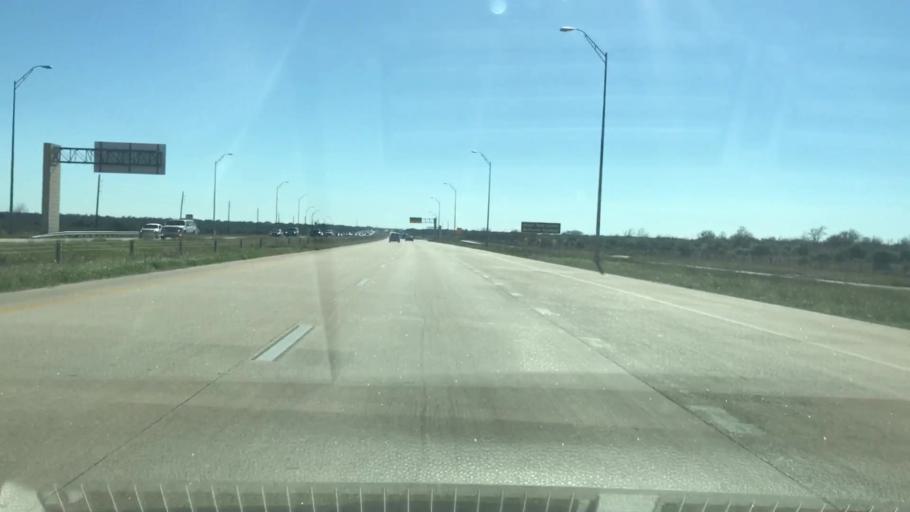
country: US
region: Texas
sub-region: Harris County
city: Cypress
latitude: 29.9862
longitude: -95.7696
